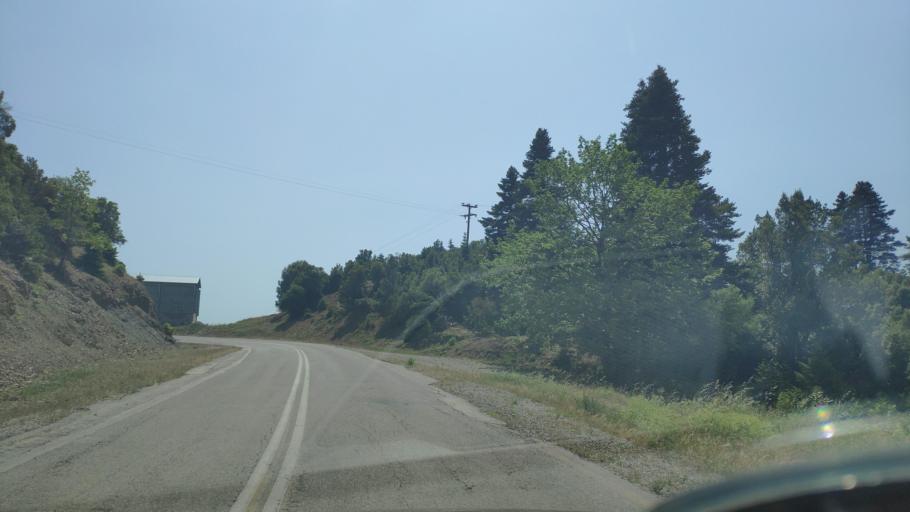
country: GR
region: Epirus
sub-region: Nomos Artas
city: Ano Kalentini
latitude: 39.2410
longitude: 21.2315
